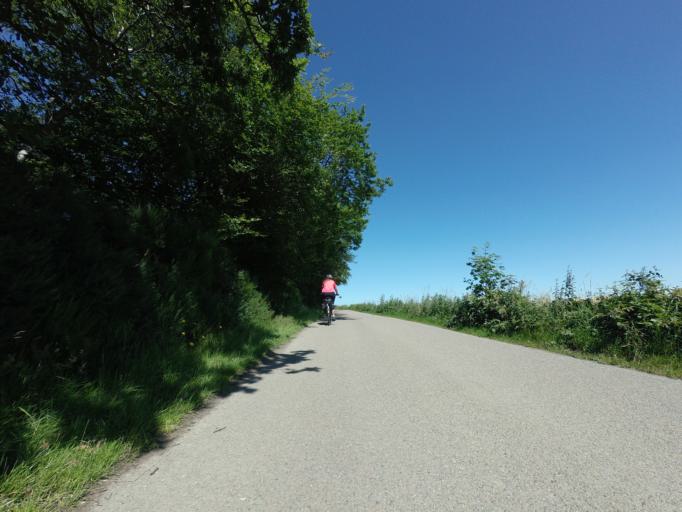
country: GB
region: Scotland
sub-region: Aberdeenshire
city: Macduff
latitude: 57.6452
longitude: -2.5054
